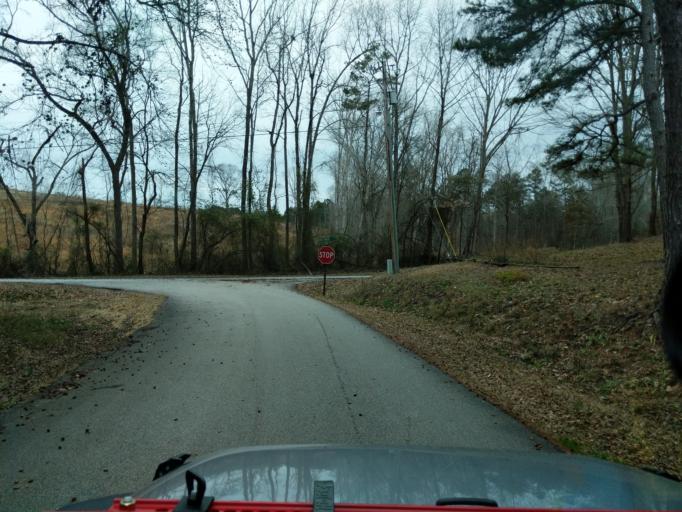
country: US
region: Georgia
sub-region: Franklin County
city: Gumlog
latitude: 34.4788
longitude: -83.0285
